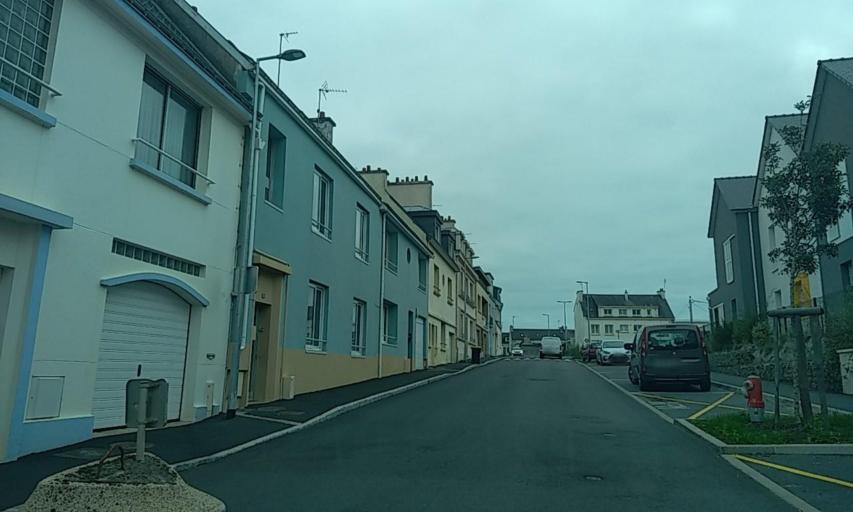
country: FR
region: Brittany
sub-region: Departement du Morbihan
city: Lorient
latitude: 47.7666
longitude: -3.3599
